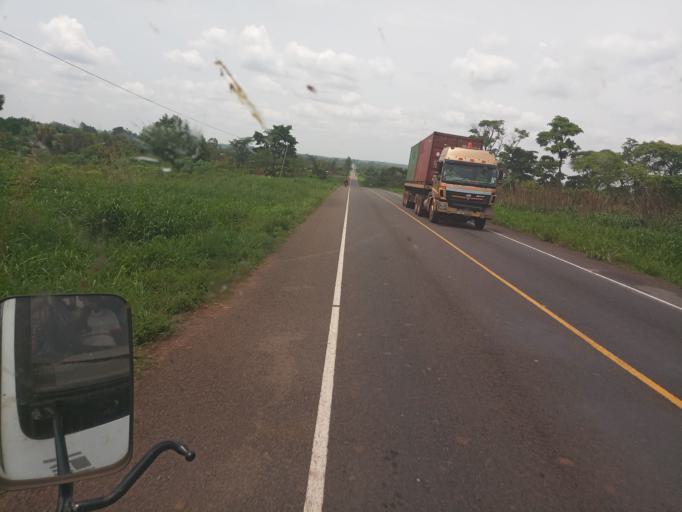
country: UG
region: Northern Region
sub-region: Oyam District
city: Oyam
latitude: 2.1810
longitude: 32.2259
